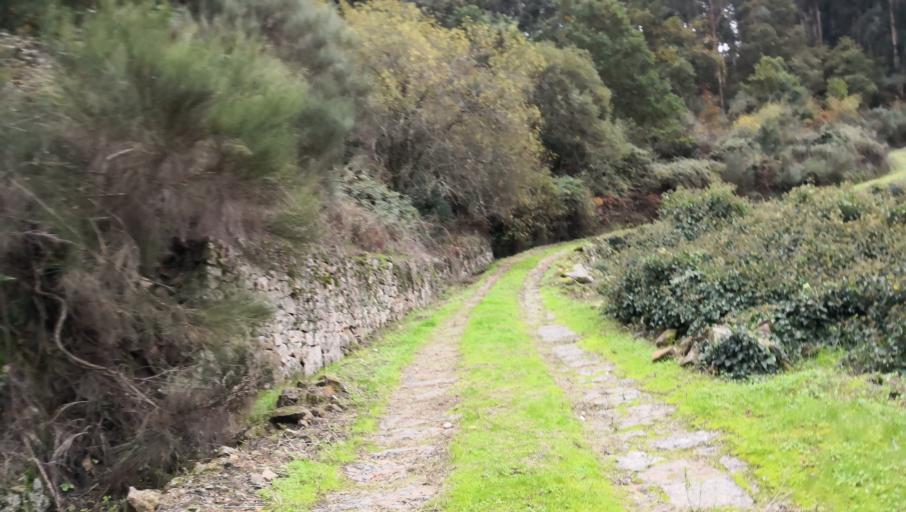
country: PT
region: Vila Real
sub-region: Vila Real
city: Vila Real
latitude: 41.2878
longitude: -7.7471
